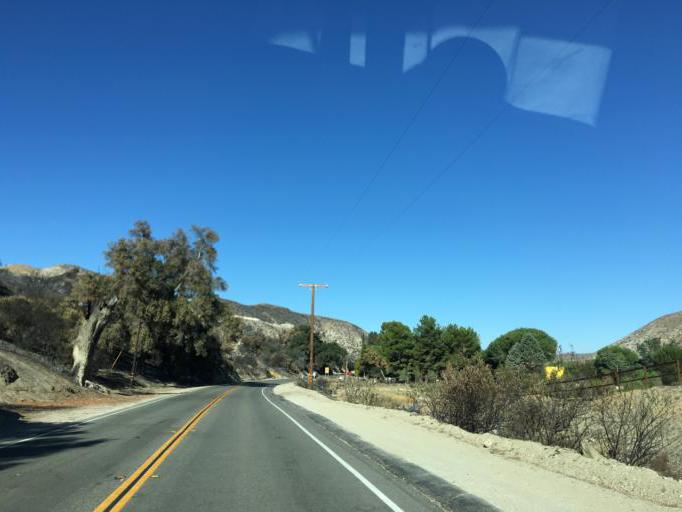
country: US
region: California
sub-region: Los Angeles County
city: Acton
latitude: 34.4380
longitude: -118.2634
